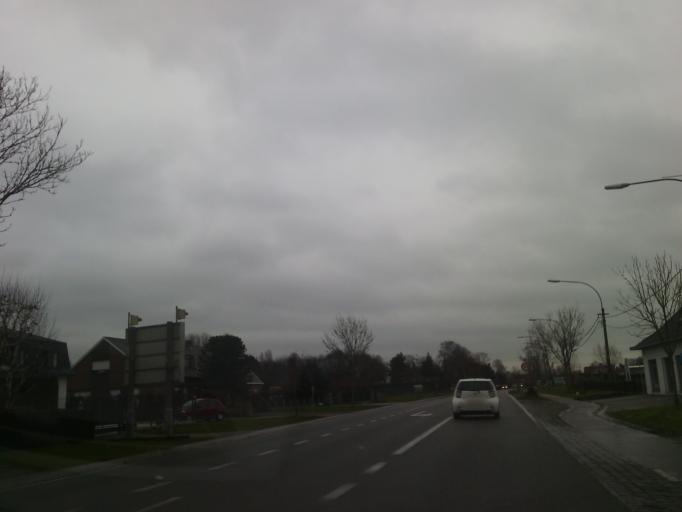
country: BE
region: Flanders
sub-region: Provincie Oost-Vlaanderen
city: Laarne
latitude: 51.0426
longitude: 3.8818
